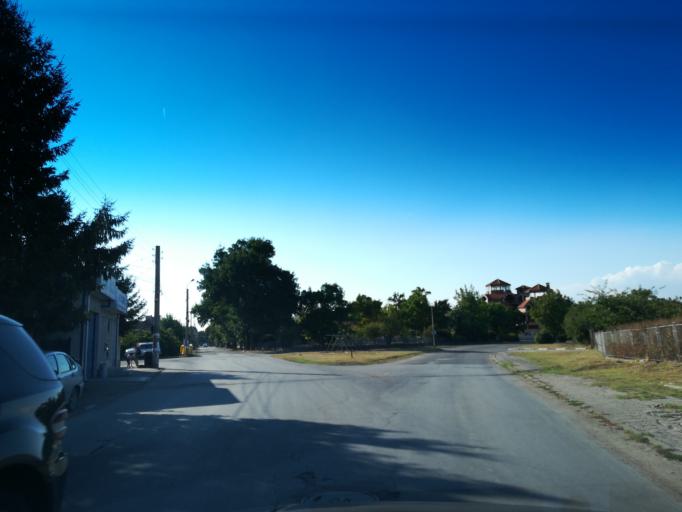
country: BG
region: Stara Zagora
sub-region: Obshtina Chirpan
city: Chirpan
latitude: 42.0952
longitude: 25.2329
